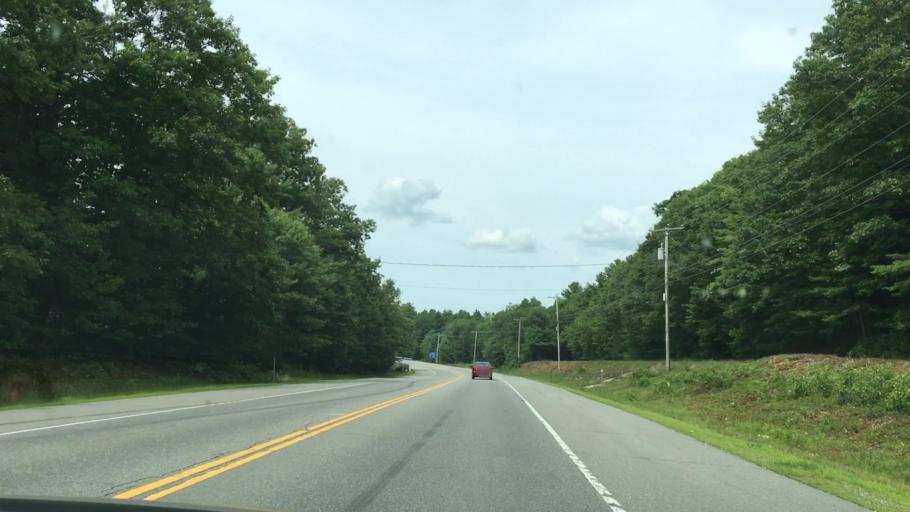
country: US
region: New Hampshire
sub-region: Cheshire County
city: Rindge
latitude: 42.7732
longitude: -72.0332
